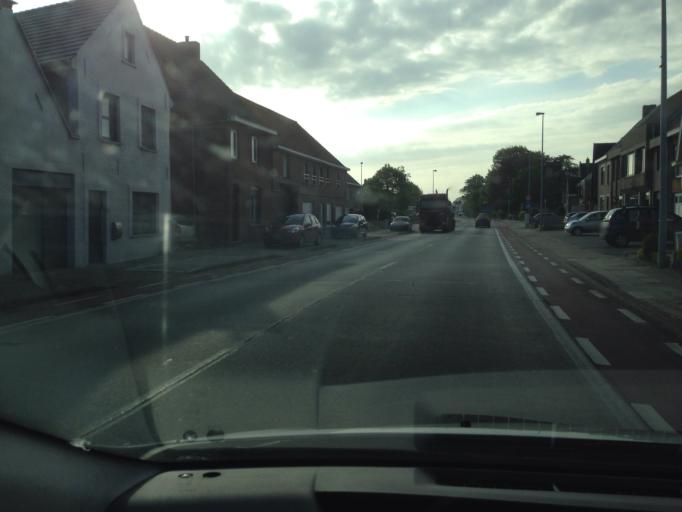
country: BE
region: Flanders
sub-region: Provincie West-Vlaanderen
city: Zedelgem
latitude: 51.1280
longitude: 3.1614
